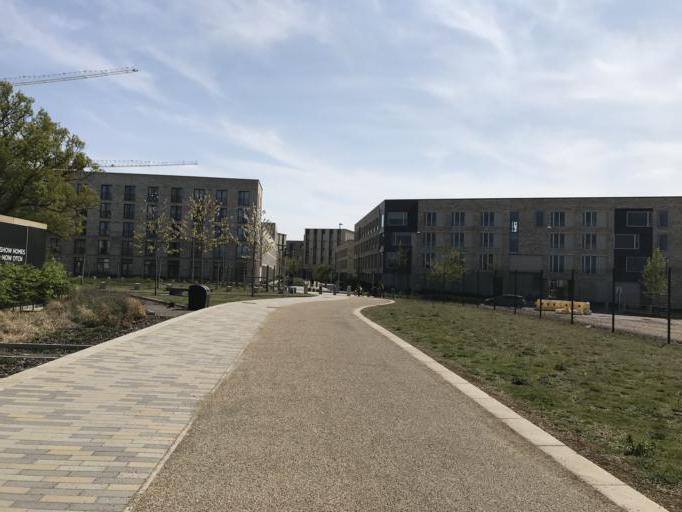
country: GB
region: England
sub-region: Cambridgeshire
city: Girton
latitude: 52.2204
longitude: 0.0853
